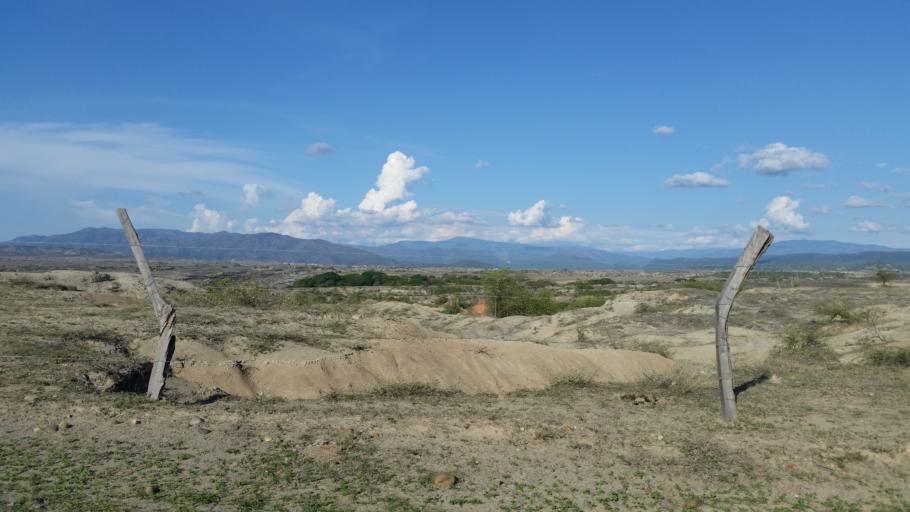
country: CO
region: Huila
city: Villavieja
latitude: 3.2318
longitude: -75.1539
